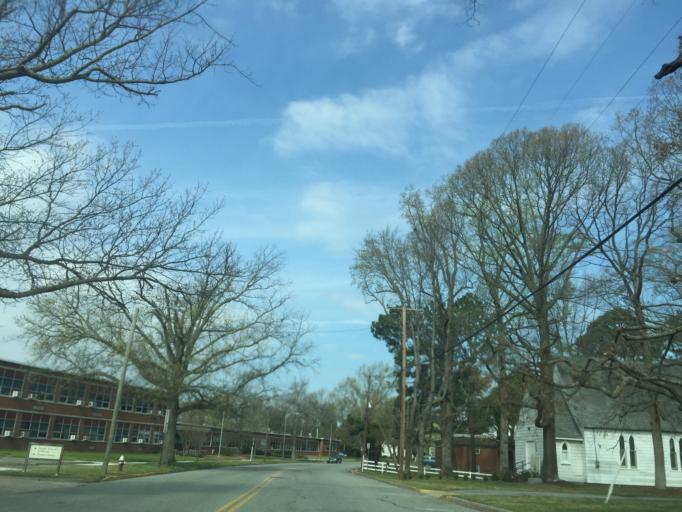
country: US
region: Virginia
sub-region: City of Newport News
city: Newport News
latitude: 37.0538
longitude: -76.4735
